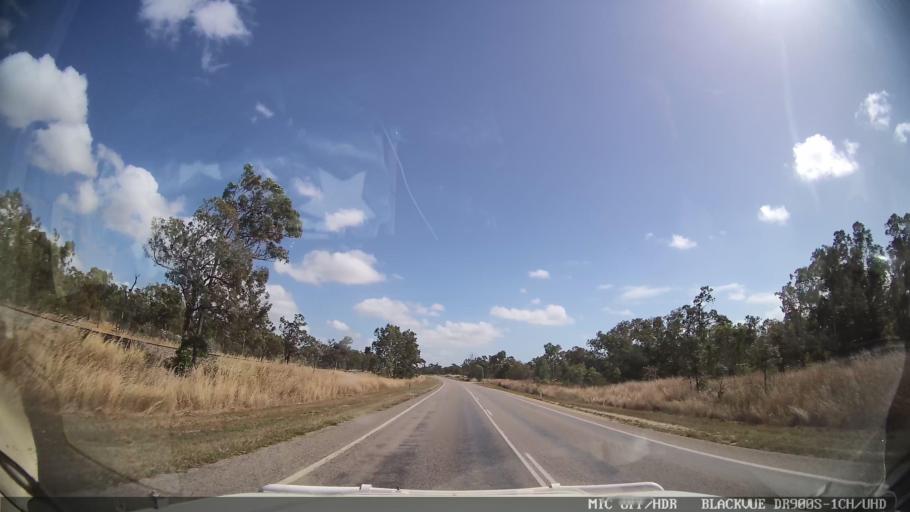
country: AU
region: Queensland
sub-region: Whitsunday
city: Bowen
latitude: -20.1787
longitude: 148.3485
